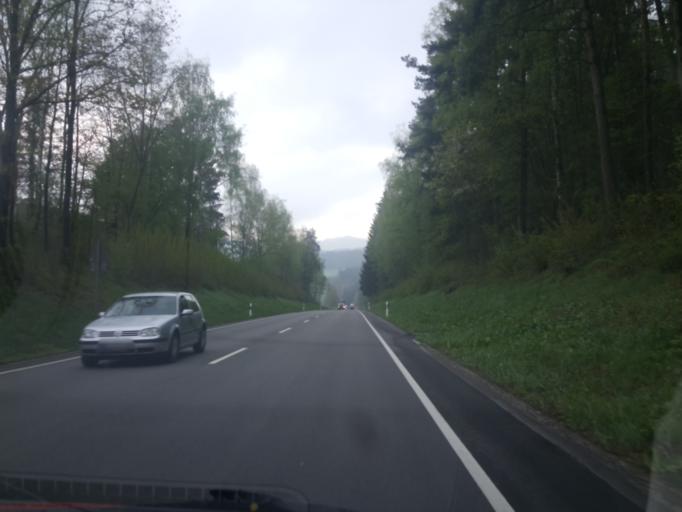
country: DE
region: Bavaria
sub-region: Lower Bavaria
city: Viechtach
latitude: 49.0612
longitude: 12.9055
